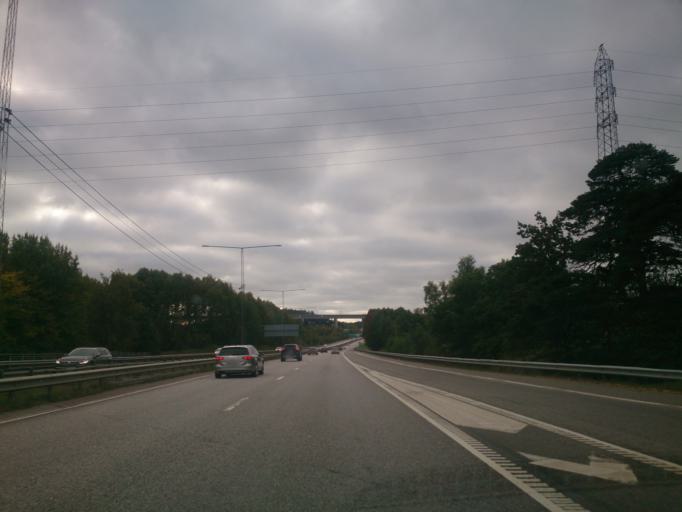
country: SE
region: Stockholm
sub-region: Sodertalje Kommun
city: Pershagen
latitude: 59.1735
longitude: 17.6461
